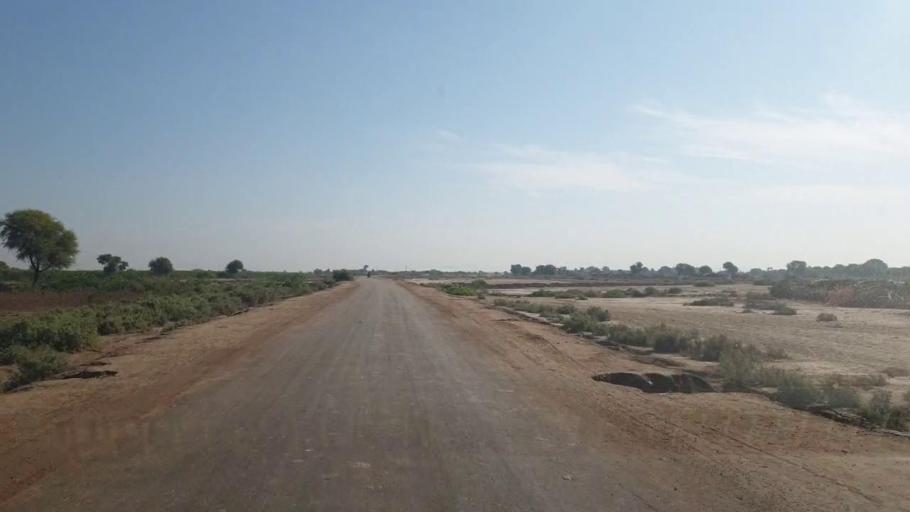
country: PK
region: Sindh
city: Rajo Khanani
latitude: 24.9237
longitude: 68.9369
